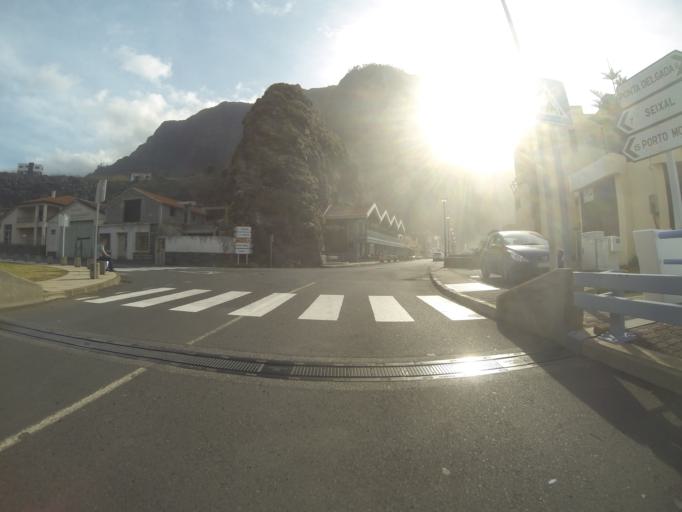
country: PT
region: Madeira
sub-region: Sao Vicente
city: Sao Vicente
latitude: 32.8081
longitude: -17.0480
